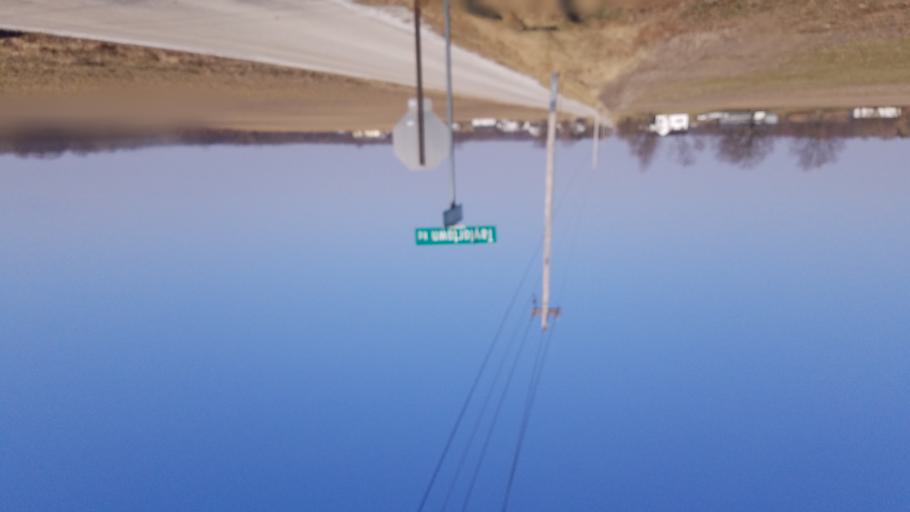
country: US
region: Ohio
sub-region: Richland County
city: Ontario
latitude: 40.8578
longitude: -82.5521
